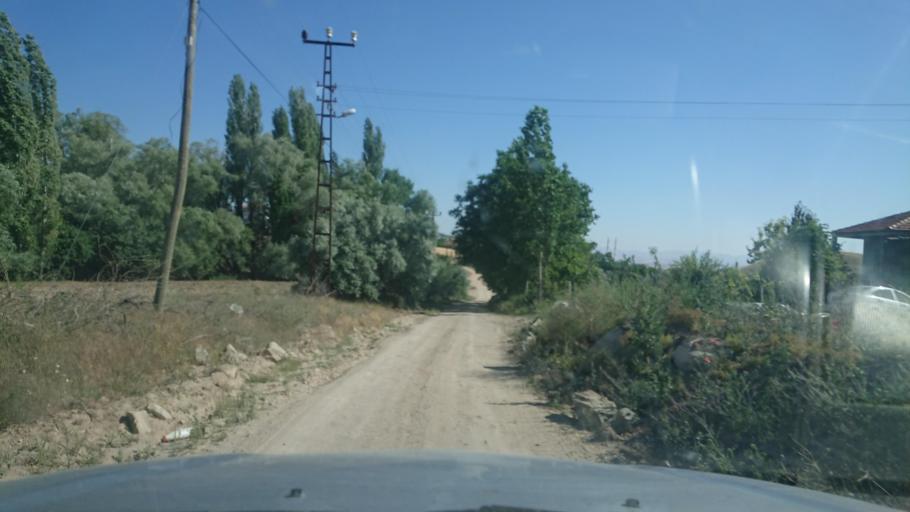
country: TR
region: Aksaray
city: Agacoren
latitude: 38.8617
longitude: 33.9123
